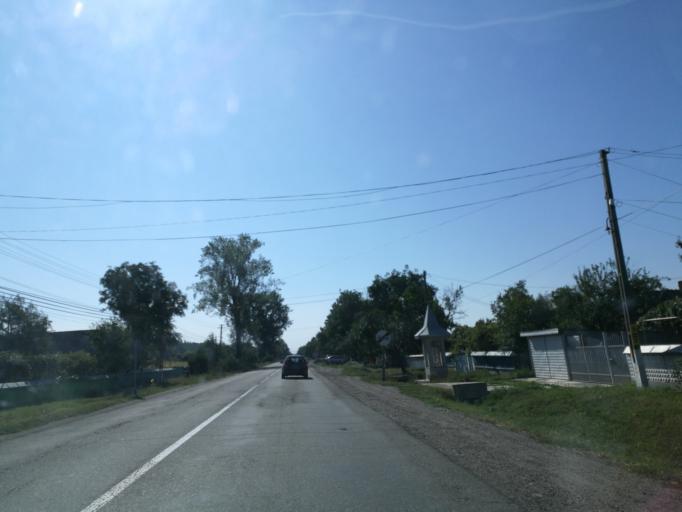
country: RO
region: Iasi
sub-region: Comuna Miroslavesti
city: Miroslavesti
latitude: 47.1577
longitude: 26.6366
